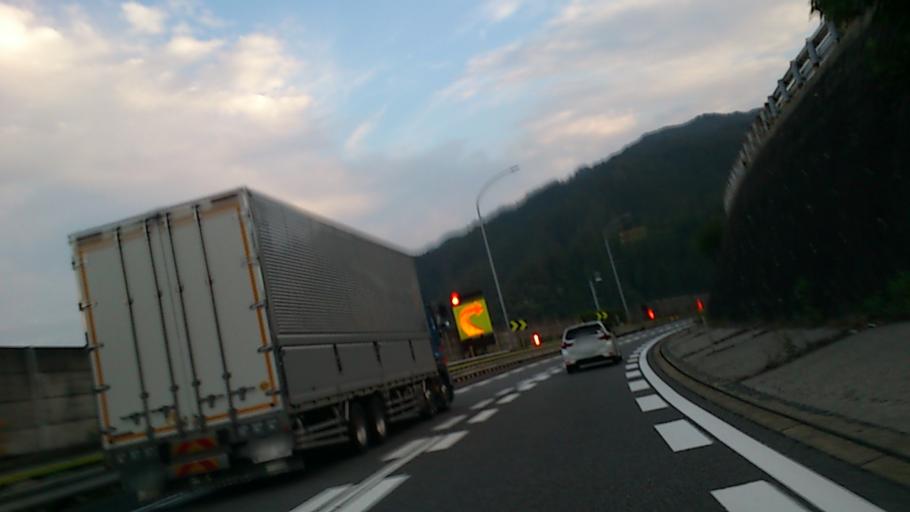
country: JP
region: Nagano
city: Iida
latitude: 35.4475
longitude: 137.7443
